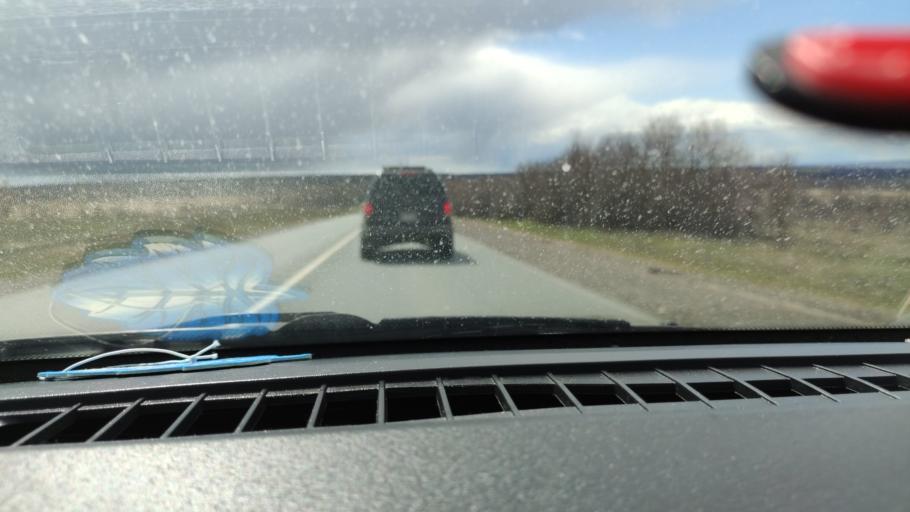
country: RU
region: Samara
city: Zhigulevsk
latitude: 53.3034
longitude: 49.3477
